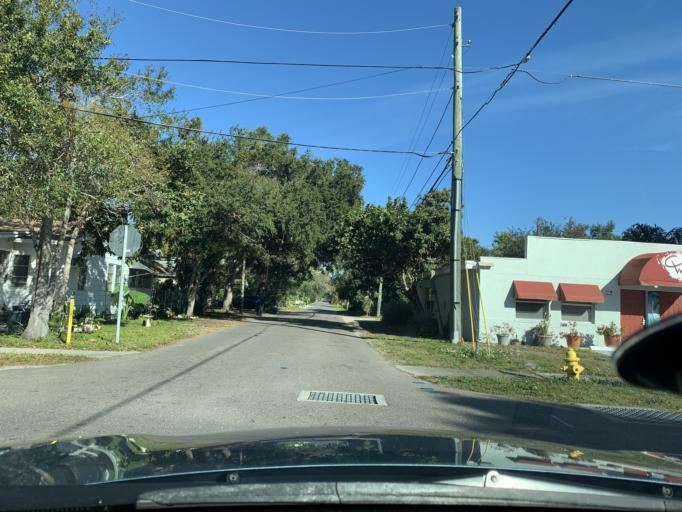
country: US
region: Florida
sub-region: Pinellas County
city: Gulfport
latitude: 27.7521
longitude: -82.7017
